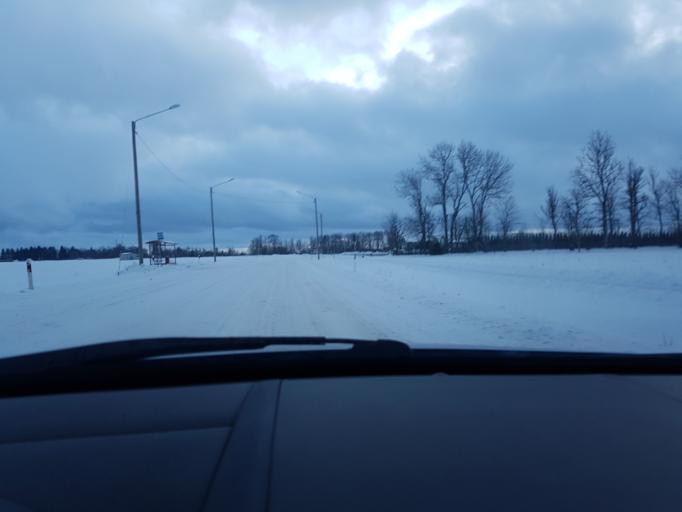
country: EE
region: Harju
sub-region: Kiili vald
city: Kiili
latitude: 59.3436
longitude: 24.8078
